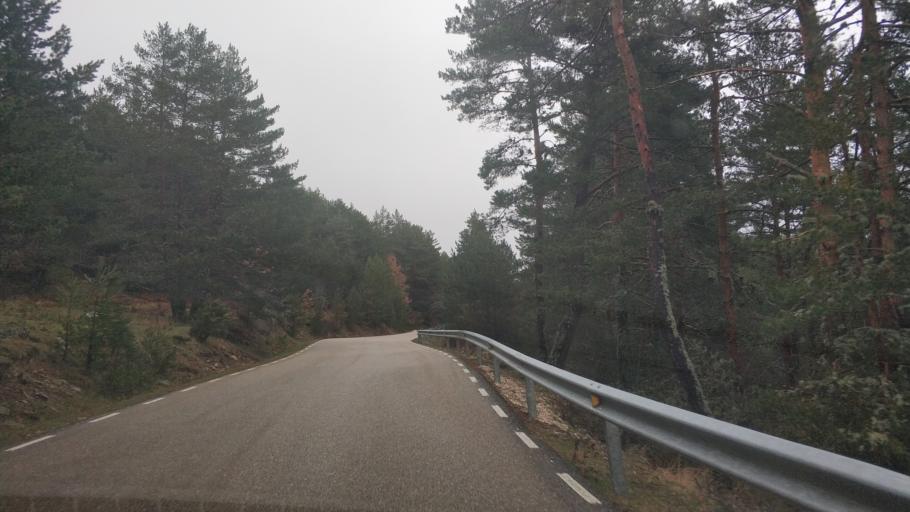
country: ES
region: Castille and Leon
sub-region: Provincia de Burgos
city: Quintanar de la Sierra
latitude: 42.0192
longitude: -3.0161
